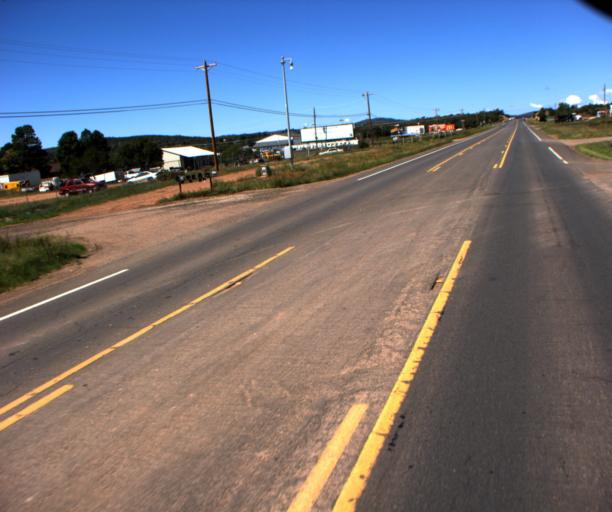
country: US
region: Arizona
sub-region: Navajo County
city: Linden
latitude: 34.2855
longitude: -110.1173
